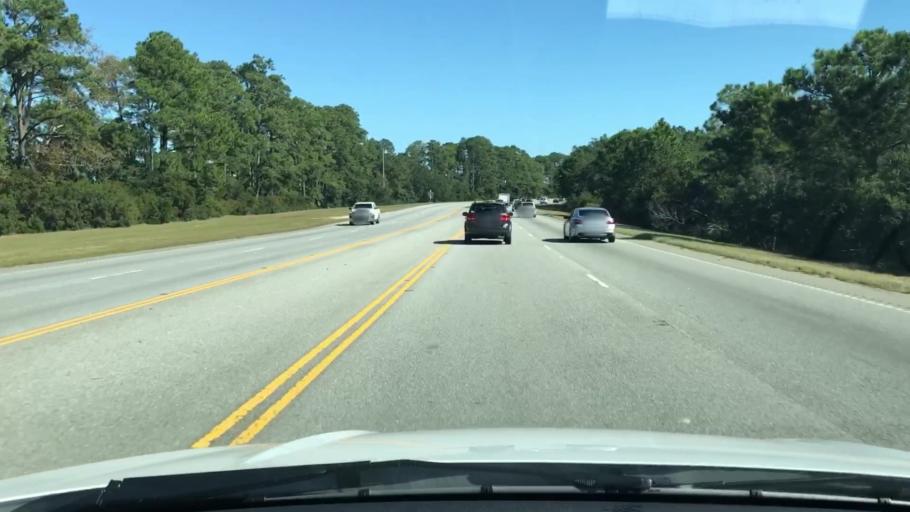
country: US
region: South Carolina
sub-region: Beaufort County
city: Laurel Bay
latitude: 32.3746
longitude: -80.8299
